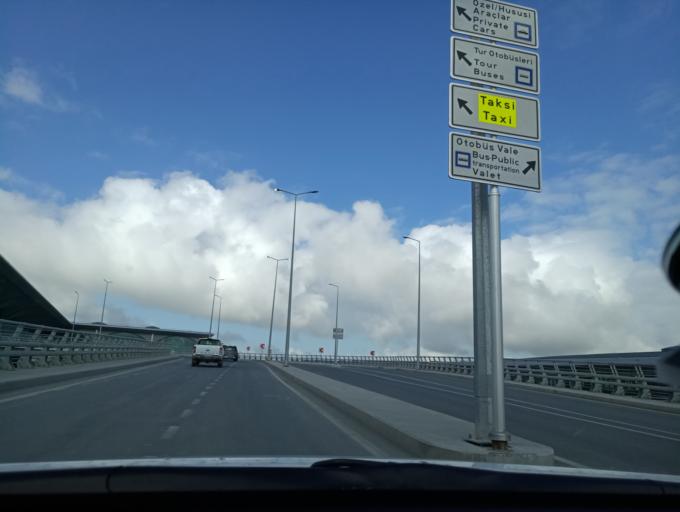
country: TR
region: Istanbul
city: Durusu
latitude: 41.2578
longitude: 28.7464
